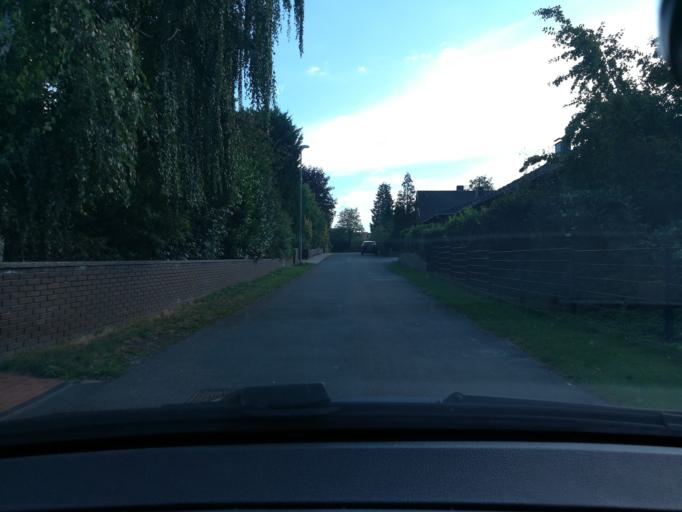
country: DE
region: North Rhine-Westphalia
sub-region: Regierungsbezirk Detmold
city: Minden
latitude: 52.3186
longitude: 8.9377
